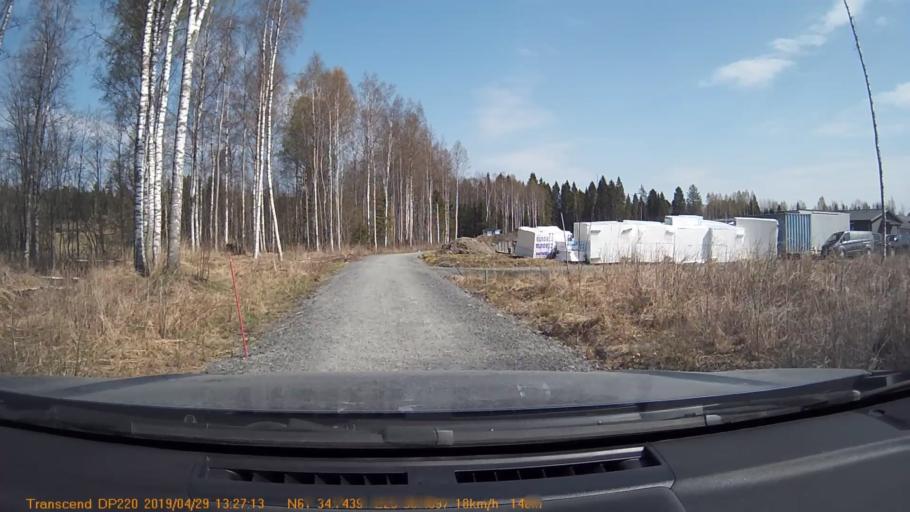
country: FI
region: Pirkanmaa
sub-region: Tampere
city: Yloejaervi
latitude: 61.5791
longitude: 23.5082
